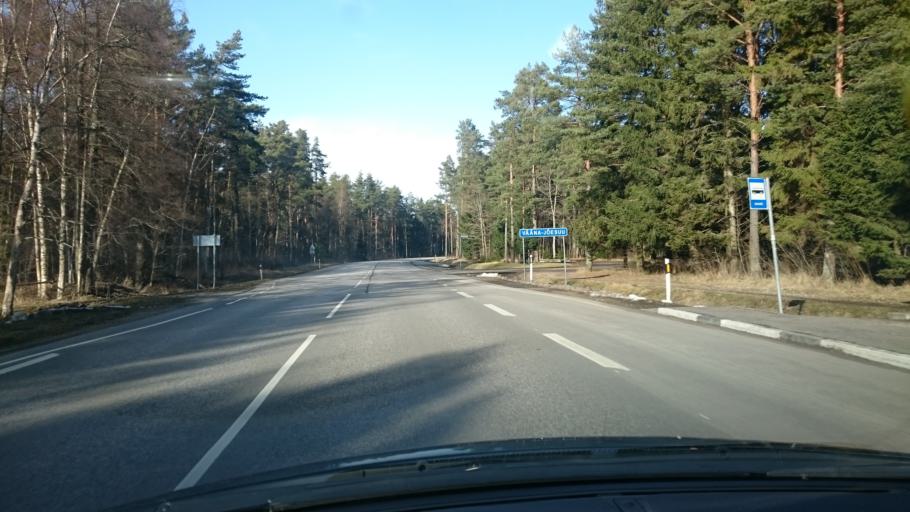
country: EE
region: Harju
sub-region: Keila linn
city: Keila
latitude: 59.4168
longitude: 24.3441
